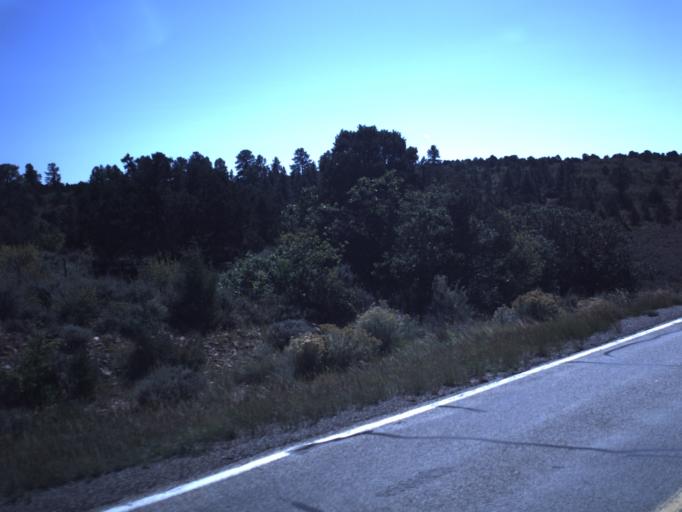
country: US
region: Utah
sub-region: Grand County
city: Moab
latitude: 38.3378
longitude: -109.2110
